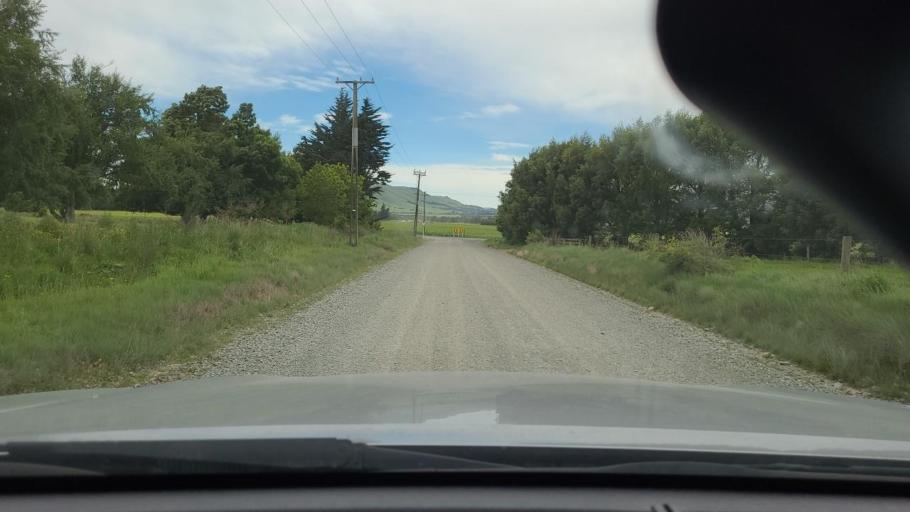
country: NZ
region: Southland
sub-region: Southland District
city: Winton
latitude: -45.6889
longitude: 168.2008
